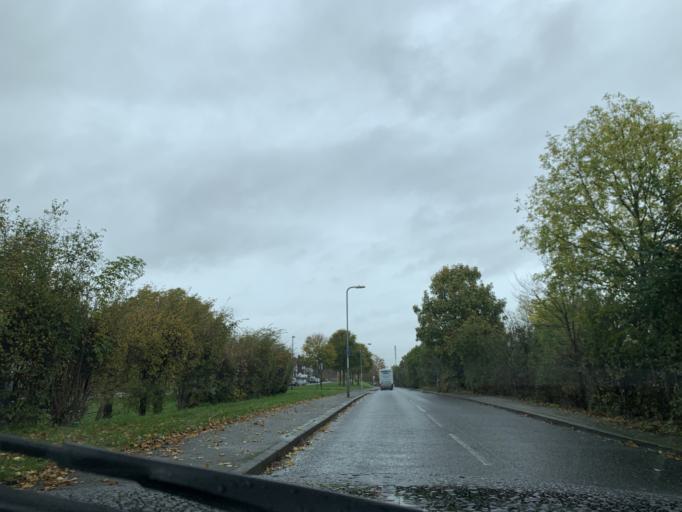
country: GB
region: England
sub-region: Greater London
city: Blackheath
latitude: 51.4435
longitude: 0.0300
